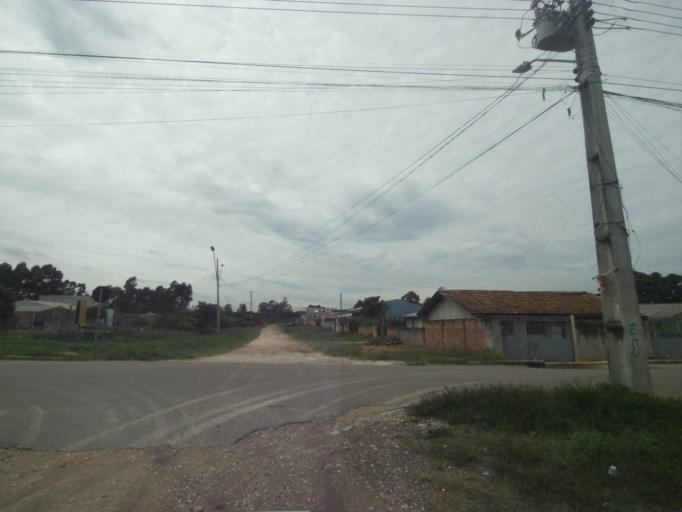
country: BR
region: Parana
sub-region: Pinhais
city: Pinhais
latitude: -25.4740
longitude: -49.1896
